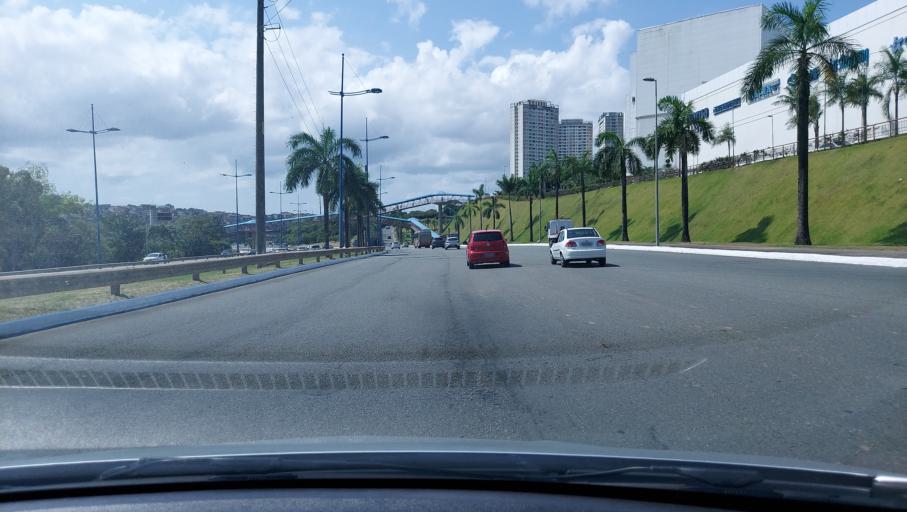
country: BR
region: Bahia
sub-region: Salvador
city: Salvador
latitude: -12.9717
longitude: -38.4753
